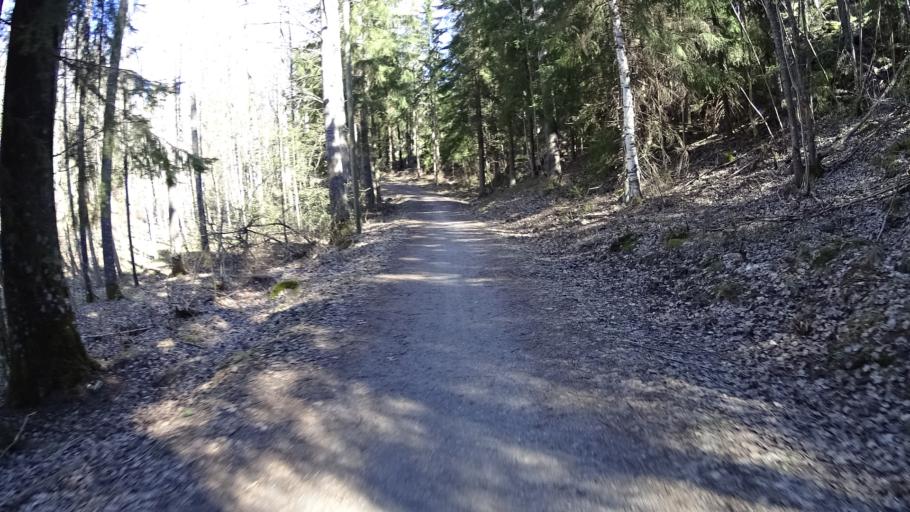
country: FI
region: Uusimaa
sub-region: Helsinki
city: Espoo
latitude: 60.2303
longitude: 24.6544
